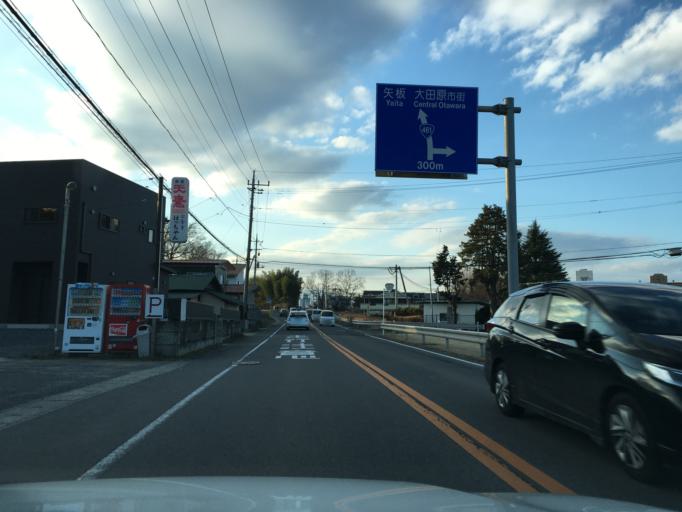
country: JP
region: Tochigi
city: Otawara
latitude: 36.8632
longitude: 140.0848
